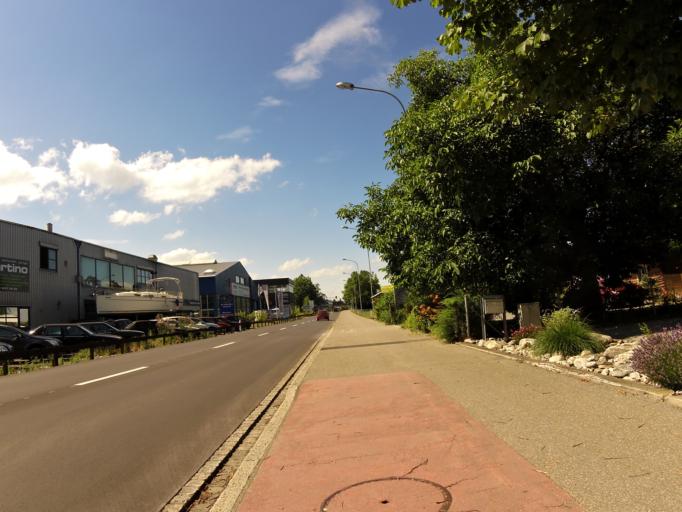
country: CH
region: Saint Gallen
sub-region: Wahlkreis Rorschach
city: Goldach
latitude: 47.4866
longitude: 9.4760
